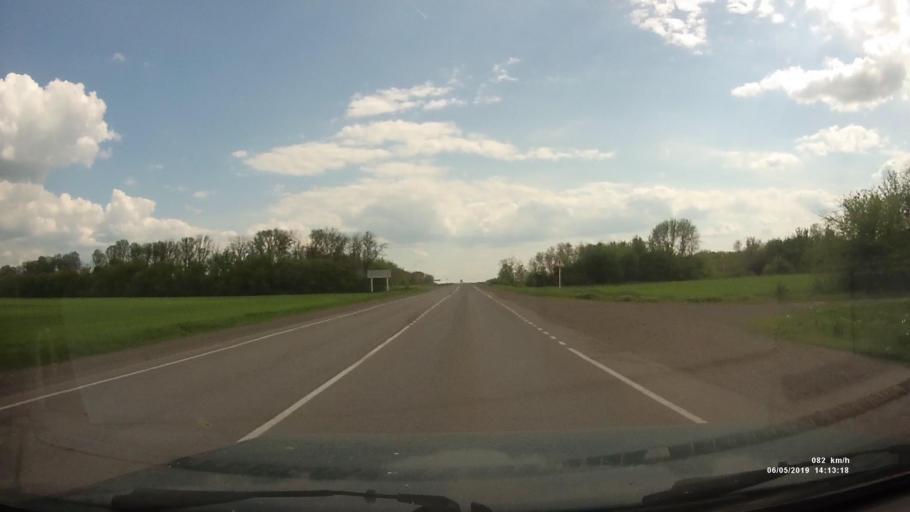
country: RU
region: Rostov
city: Kamenolomni
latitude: 47.6624
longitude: 40.2917
